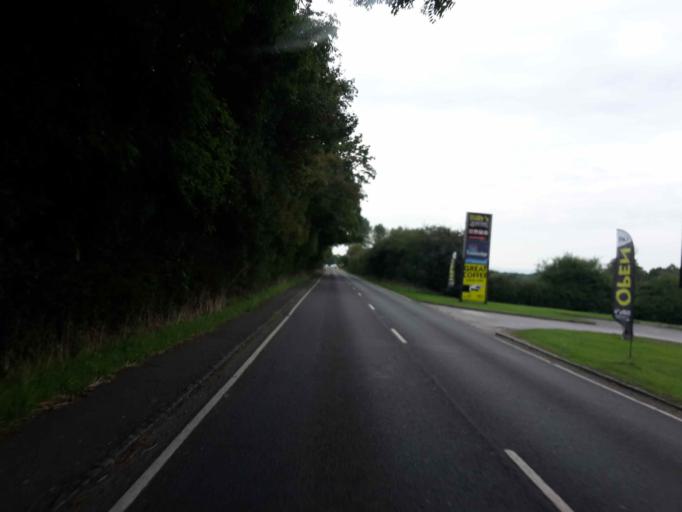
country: GB
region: England
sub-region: West Sussex
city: Billingshurst
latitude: 51.0380
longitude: -0.4403
